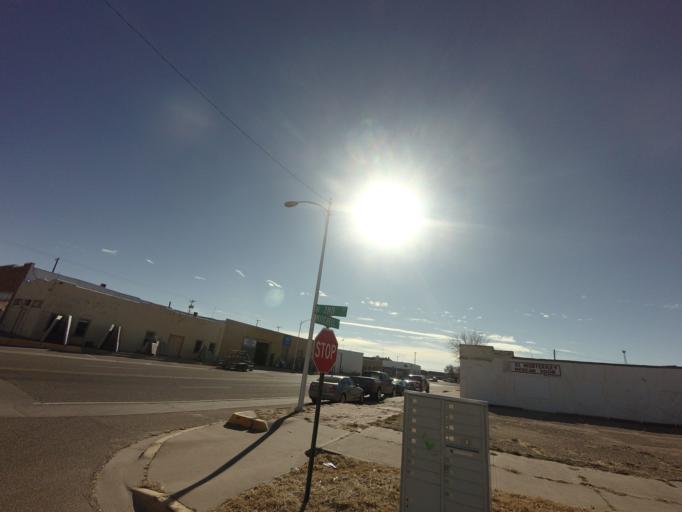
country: US
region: New Mexico
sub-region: Curry County
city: Clovis
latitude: 34.3997
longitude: -103.2068
